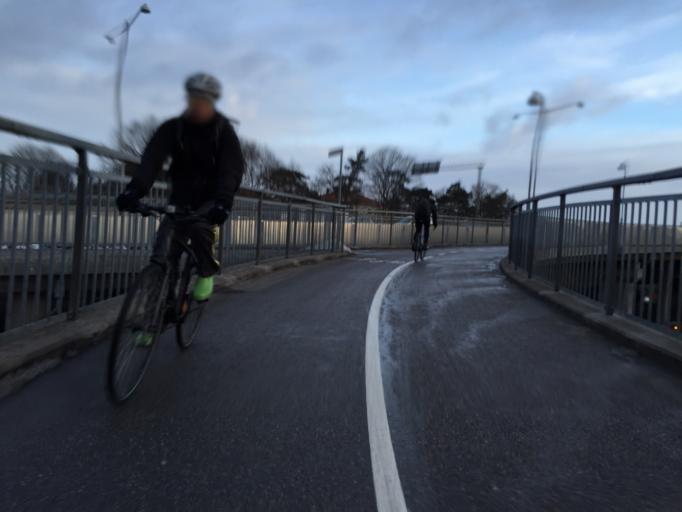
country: SE
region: Stockholm
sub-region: Solna Kommun
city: Solna
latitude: 59.3331
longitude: 17.9901
